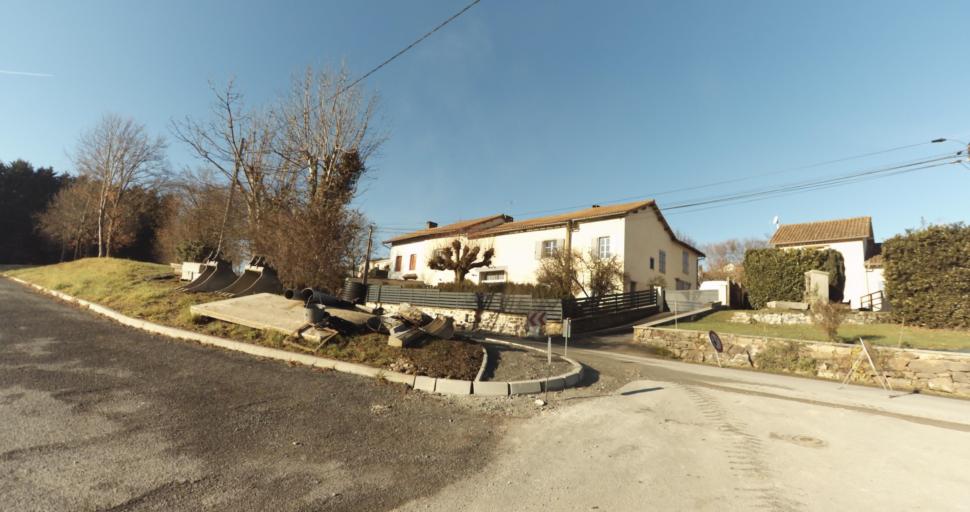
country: FR
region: Limousin
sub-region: Departement de la Haute-Vienne
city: Aixe-sur-Vienne
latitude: 45.7985
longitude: 1.1506
